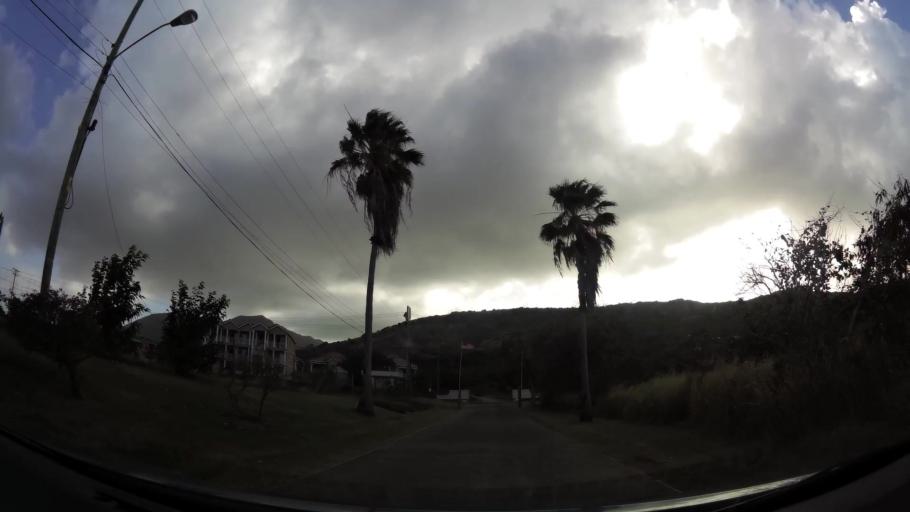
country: KN
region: Saint James Windwa
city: Newcastle
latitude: 17.1912
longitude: -62.5628
